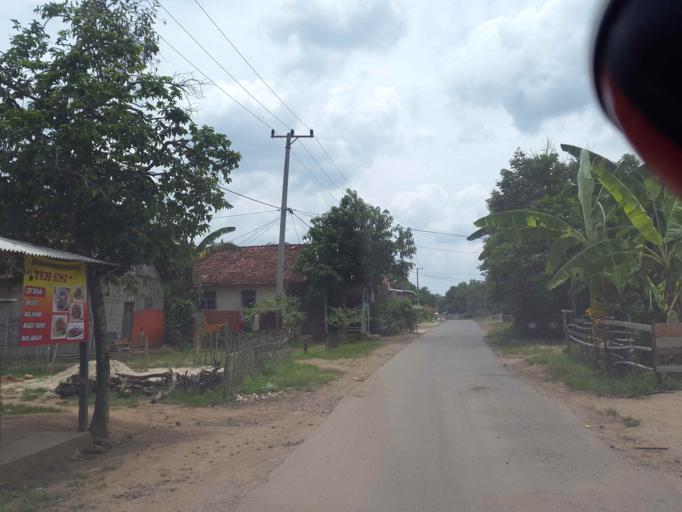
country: ID
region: Lampung
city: Natar
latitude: -5.3138
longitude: 105.2287
